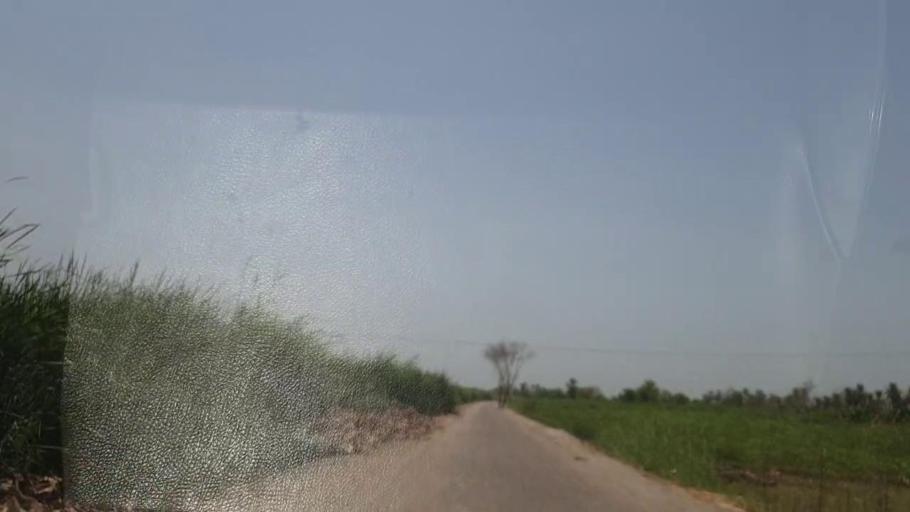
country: PK
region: Sindh
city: Bozdar
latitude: 27.2500
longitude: 68.6587
